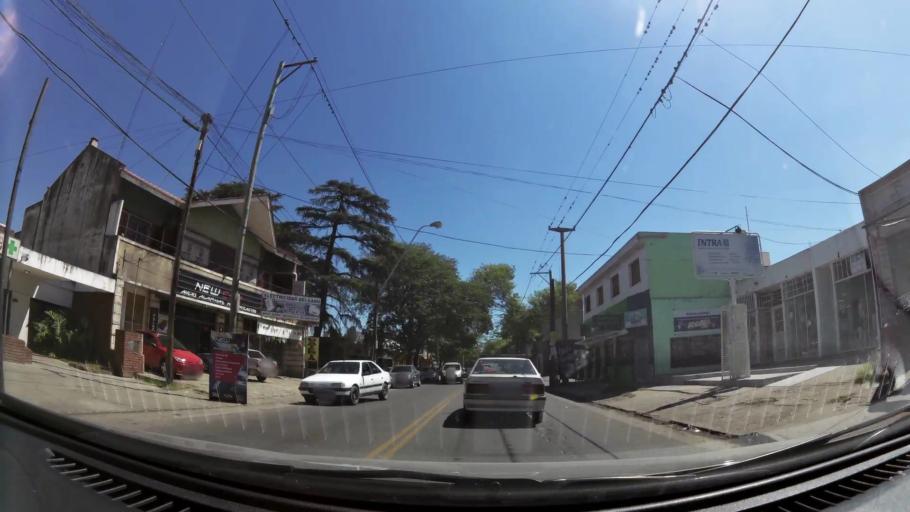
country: AR
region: Cordoba
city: Villa Allende
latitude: -31.3361
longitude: -64.2613
